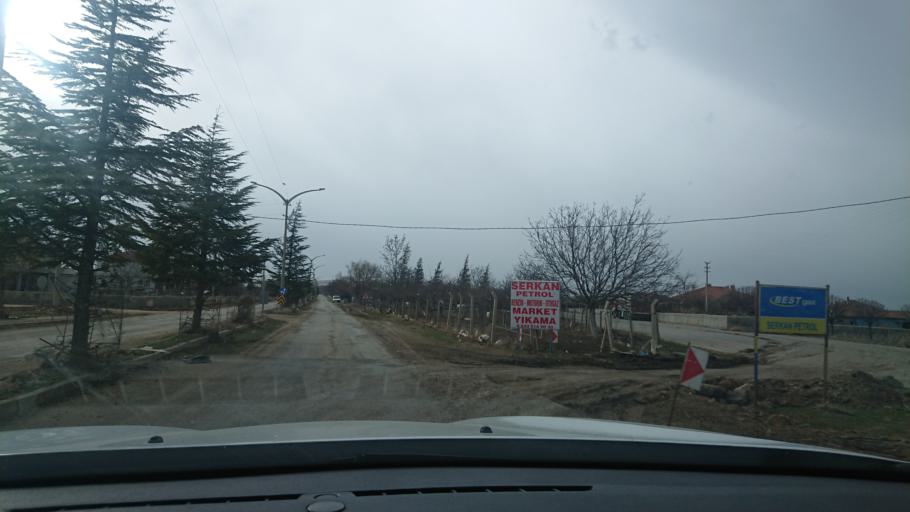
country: TR
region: Aksaray
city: Agacoren
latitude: 38.9312
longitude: 33.9669
